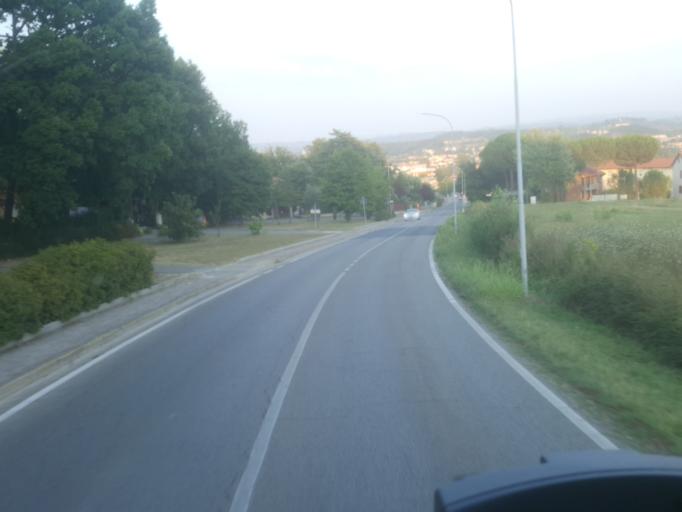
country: IT
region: Tuscany
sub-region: Province of Florence
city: Certaldo
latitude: 43.5456
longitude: 11.0226
